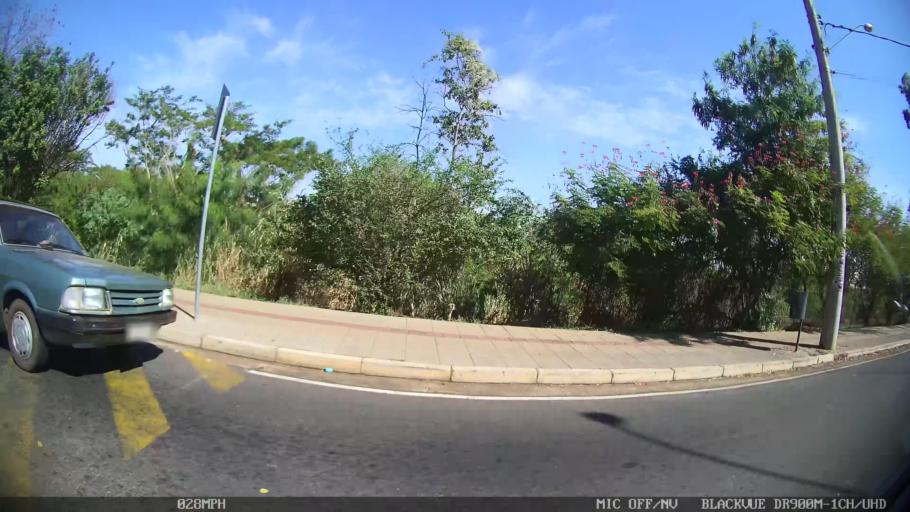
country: BR
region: Sao Paulo
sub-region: Sao Jose Do Rio Preto
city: Sao Jose do Rio Preto
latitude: -20.7758
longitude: -49.3965
